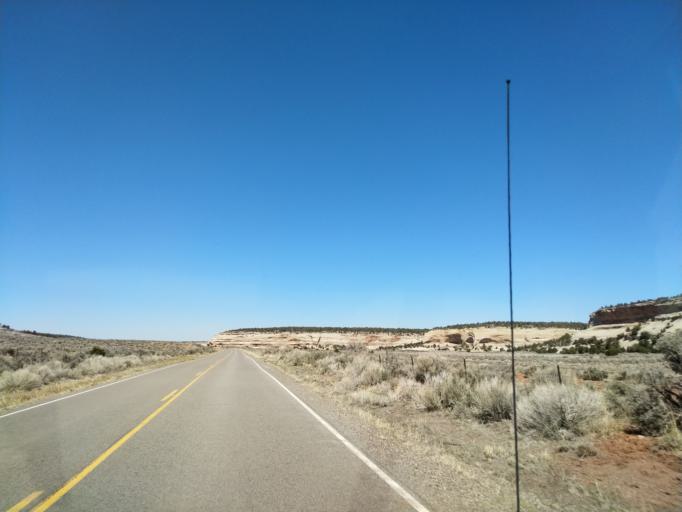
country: US
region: Colorado
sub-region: Mesa County
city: Fruita
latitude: 38.9861
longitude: -108.8115
